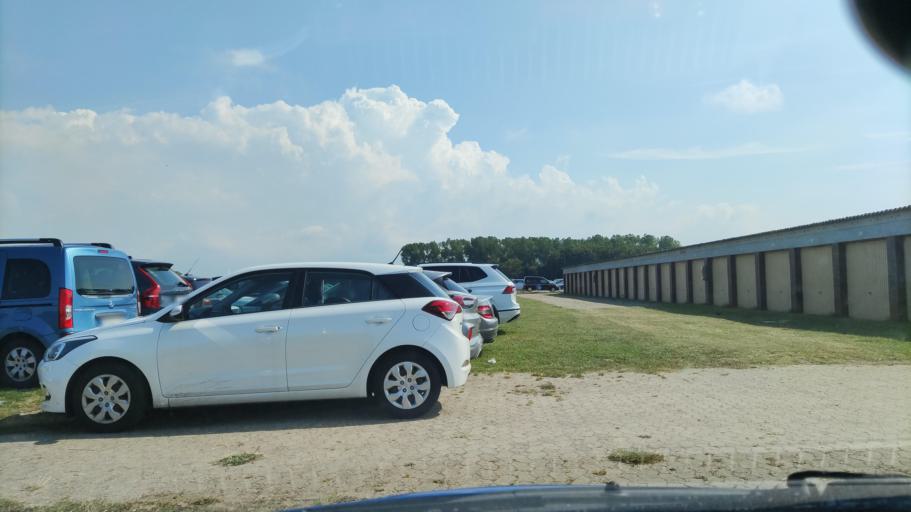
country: DE
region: Lower Saxony
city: Werdum
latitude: 53.7059
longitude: 7.8133
